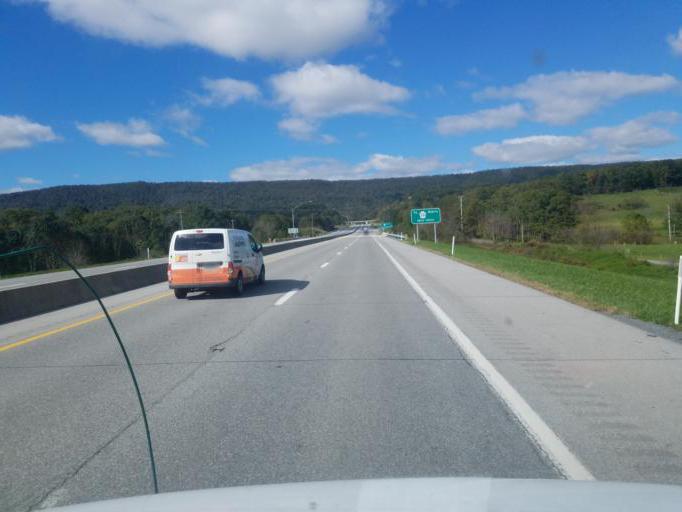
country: US
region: Pennsylvania
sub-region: Bedford County
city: Everett
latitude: 40.0226
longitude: -78.3569
